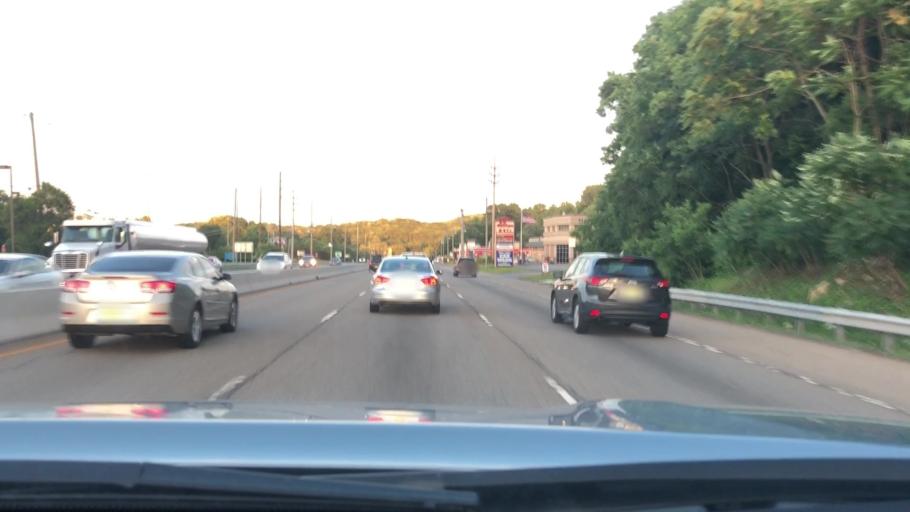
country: US
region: New Jersey
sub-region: Morris County
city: Butler
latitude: 40.9904
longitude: -74.3376
